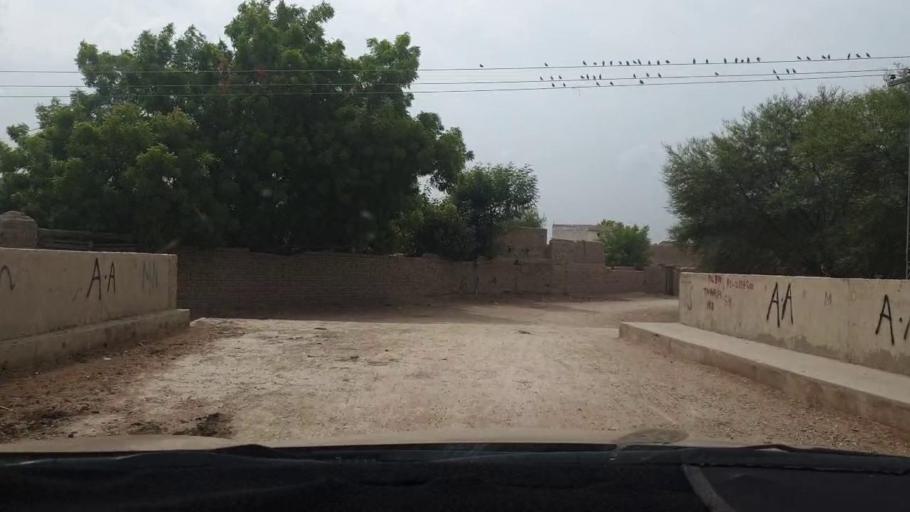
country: PK
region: Sindh
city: Naudero
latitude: 27.6269
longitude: 68.3105
